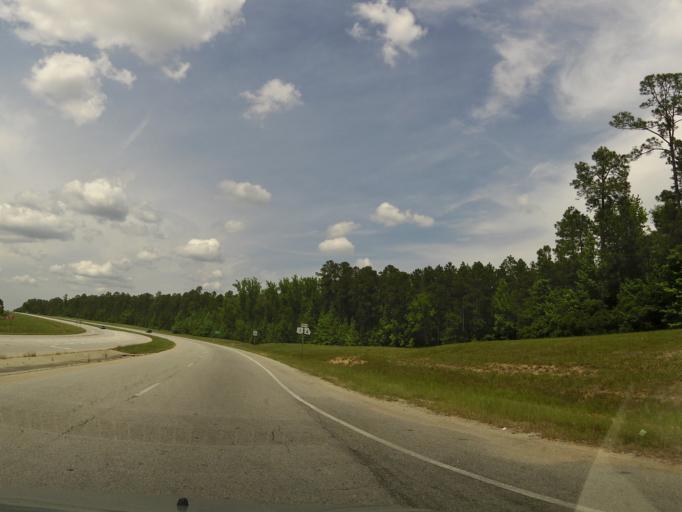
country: US
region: Georgia
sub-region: Emanuel County
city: Swainsboro
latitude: 32.6429
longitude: -82.3659
